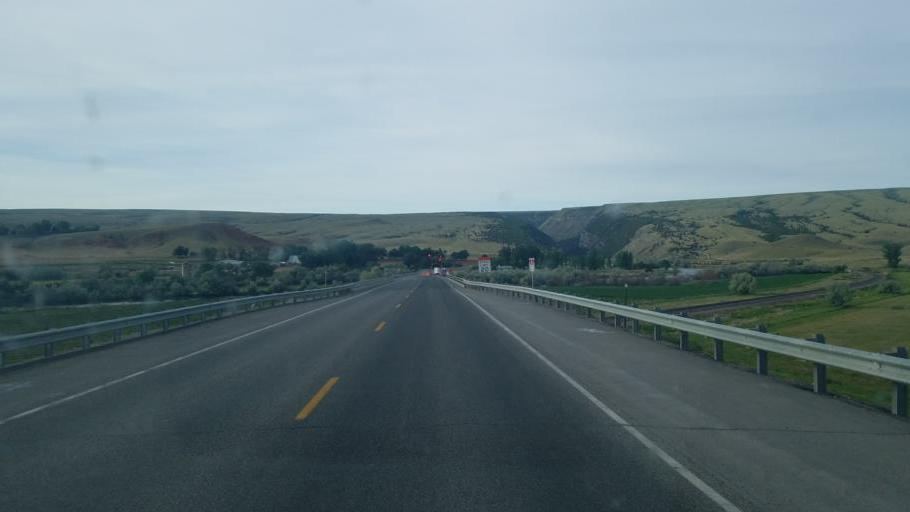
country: US
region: Wyoming
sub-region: Hot Springs County
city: Thermopolis
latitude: 43.5956
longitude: -108.2152
